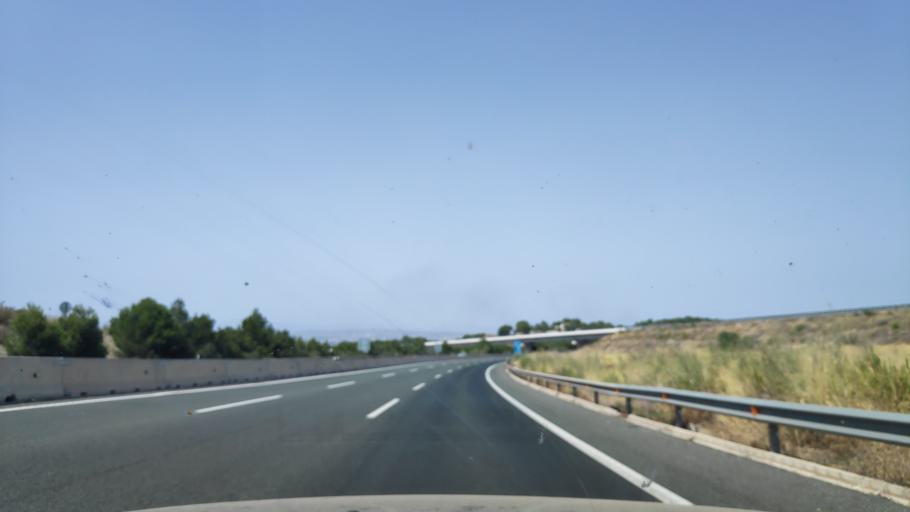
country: ES
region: Murcia
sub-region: Murcia
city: Alcantarilla
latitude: 37.9158
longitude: -1.1647
